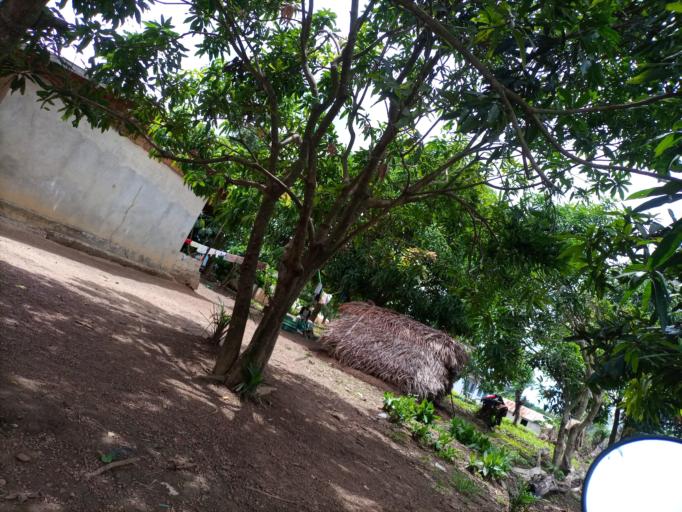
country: SL
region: Southern Province
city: Baoma
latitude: 7.9717
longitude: -11.7121
